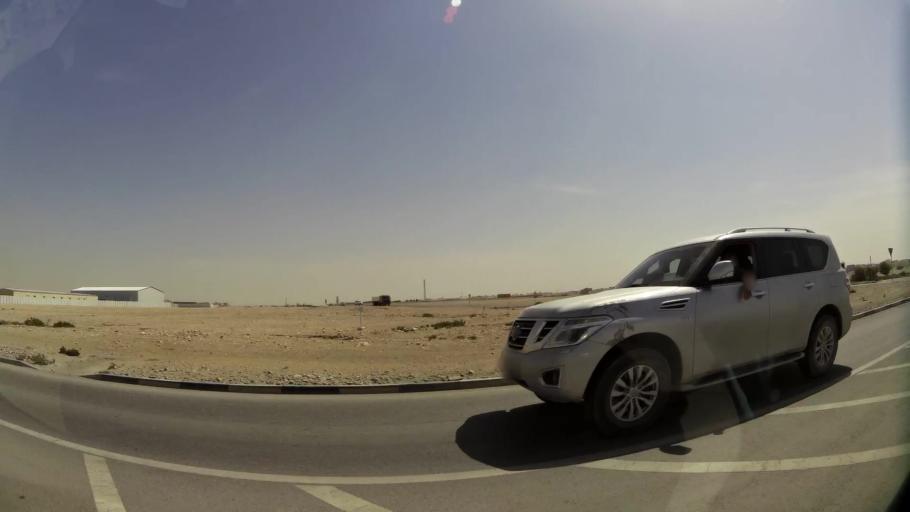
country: QA
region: Baladiyat ar Rayyan
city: Ar Rayyan
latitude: 25.2644
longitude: 51.3805
